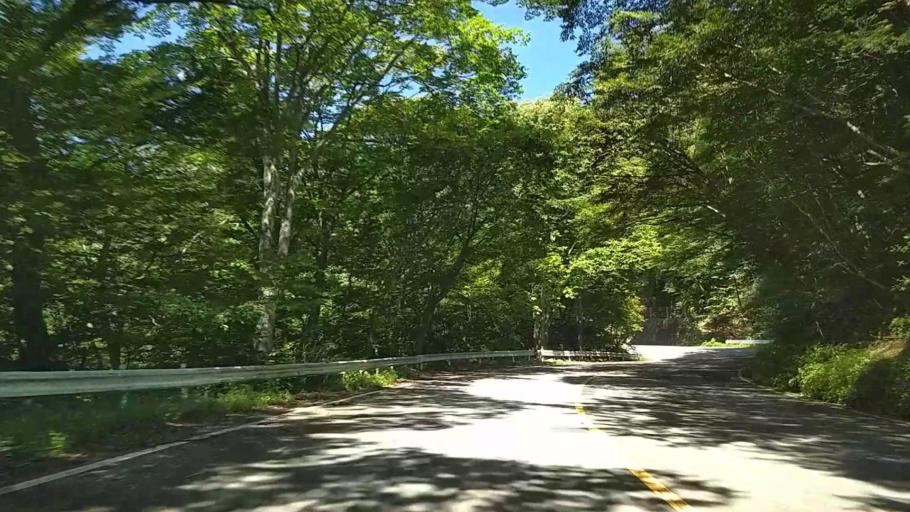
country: JP
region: Gunma
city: Annaka
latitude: 36.3537
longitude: 138.6690
